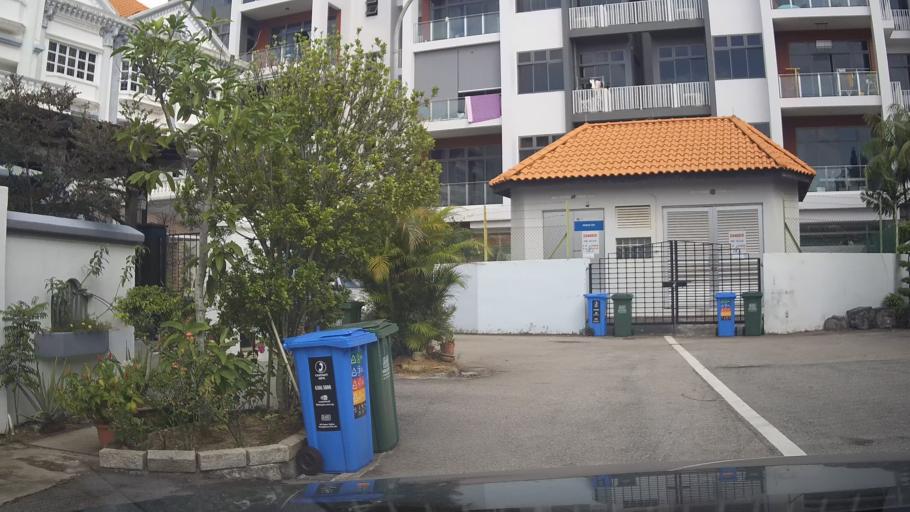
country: SG
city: Singapore
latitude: 1.3130
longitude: 103.9154
